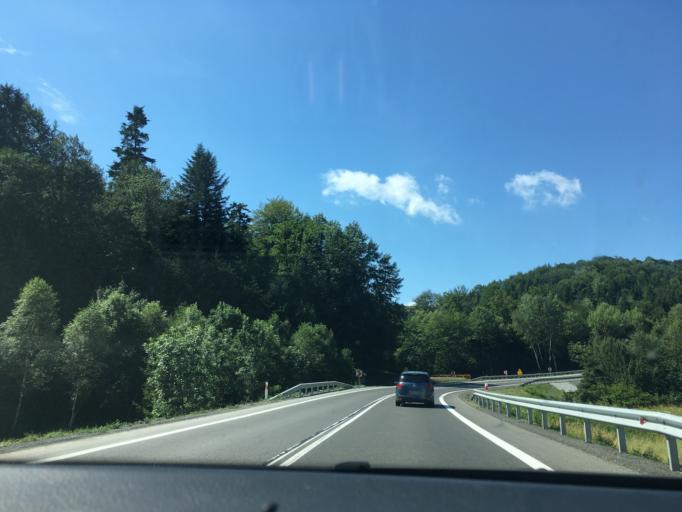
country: PL
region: Subcarpathian Voivodeship
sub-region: Powiat krosnienski
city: Dukla
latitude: 49.5236
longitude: 21.6863
